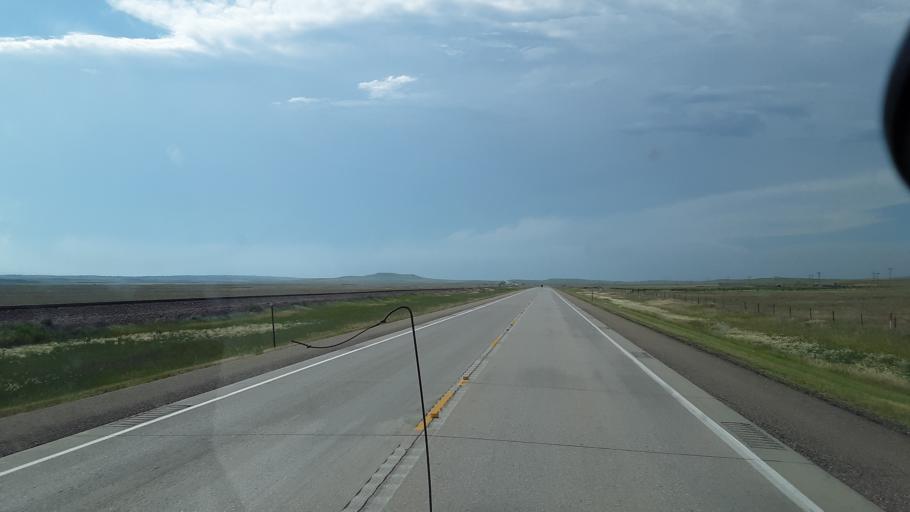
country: US
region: South Dakota
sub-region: Butte County
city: Belle Fourche
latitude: 44.7446
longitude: -103.9471
